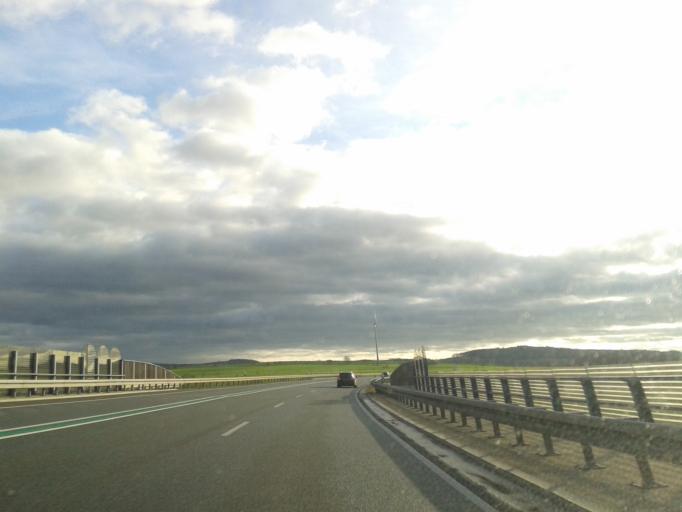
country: DE
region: Saxony
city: Lobau
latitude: 51.0770
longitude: 14.6688
